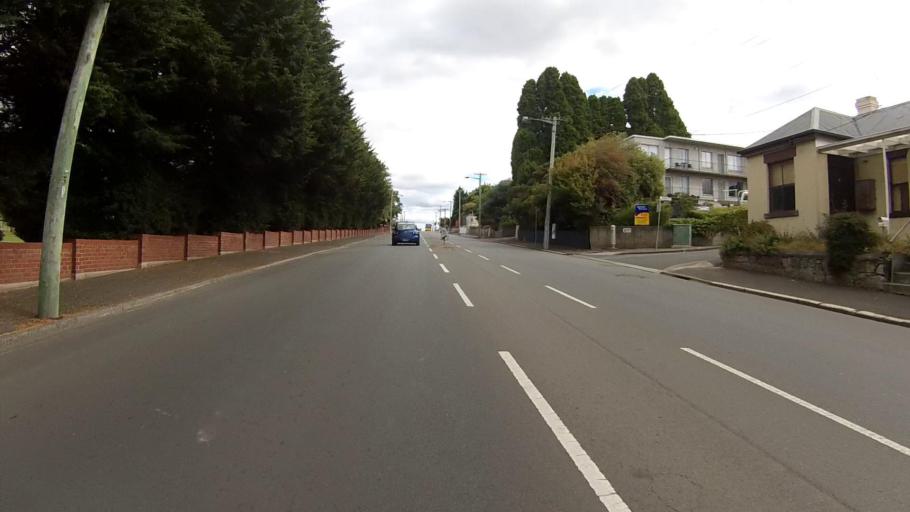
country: AU
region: Tasmania
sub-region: Hobart
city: New Town
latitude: -42.8550
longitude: 147.3025
